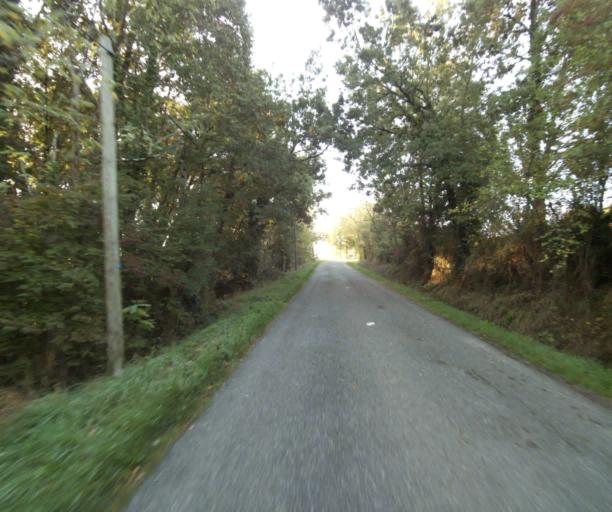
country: FR
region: Midi-Pyrenees
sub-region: Departement du Tarn-et-Garonne
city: Saint-Nauphary
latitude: 43.9362
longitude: 1.4416
